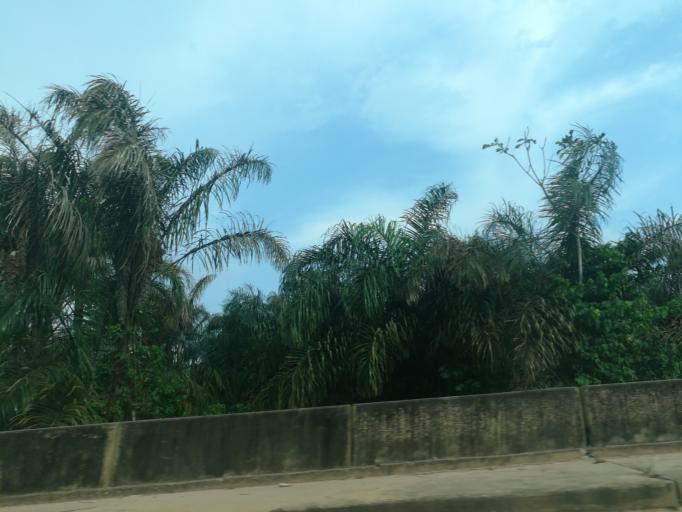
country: NG
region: Lagos
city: Ikorodu
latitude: 6.6257
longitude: 3.6639
